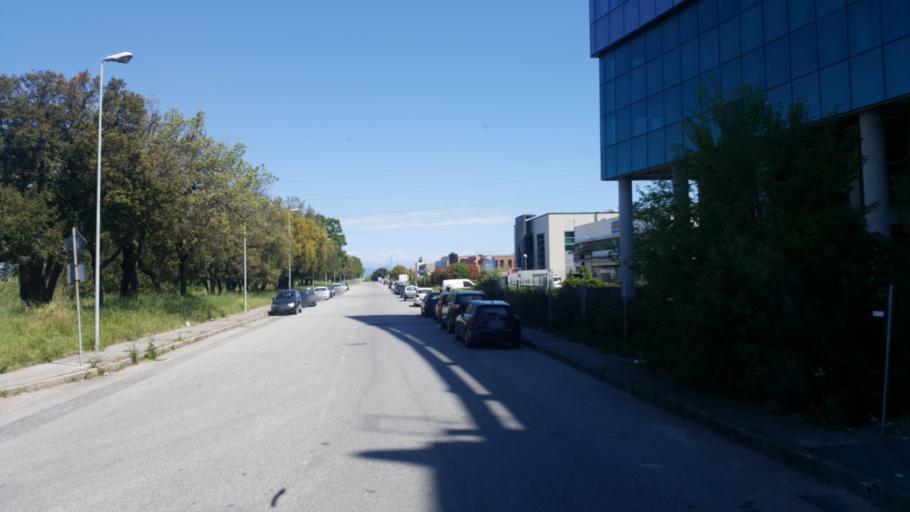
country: IT
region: Tuscany
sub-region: Provincia di Livorno
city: Livorno
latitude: 43.5703
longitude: 10.3423
